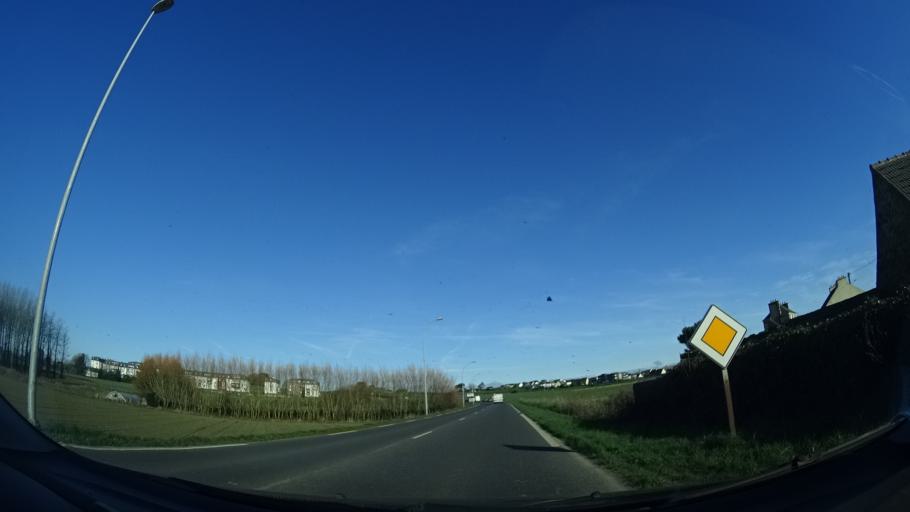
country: FR
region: Brittany
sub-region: Departement du Finistere
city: Saint-Pol-de-Leon
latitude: 48.6822
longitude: -4.0023
